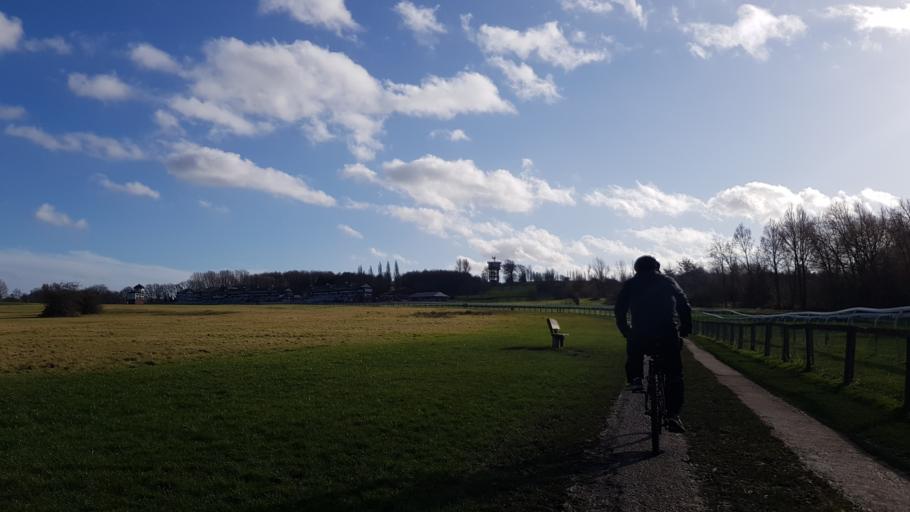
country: GB
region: England
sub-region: City and Borough of Wakefield
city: Pontefract
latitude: 53.6991
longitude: -1.3373
